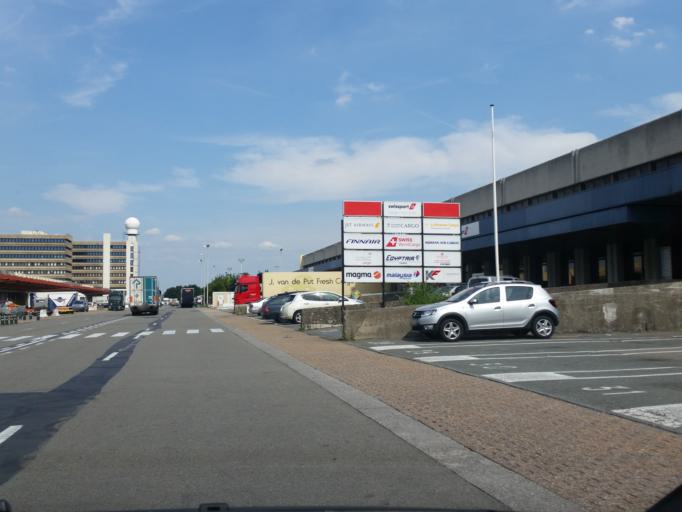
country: BE
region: Flanders
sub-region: Provincie Vlaams-Brabant
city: Machelen
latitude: 50.9038
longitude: 4.4534
